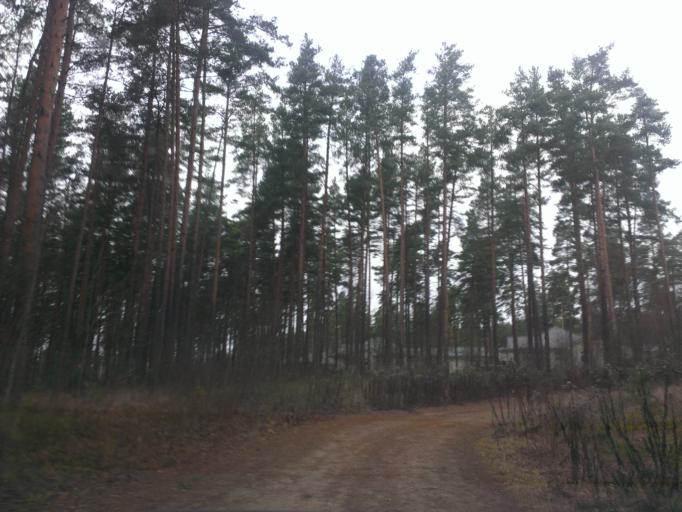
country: LV
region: Riga
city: Bergi
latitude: 56.9932
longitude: 24.3031
